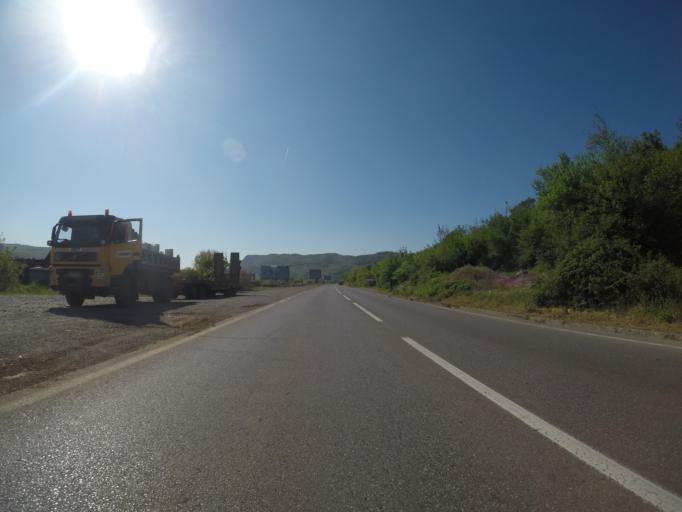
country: ME
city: Spuz
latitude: 42.4729
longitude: 19.1727
